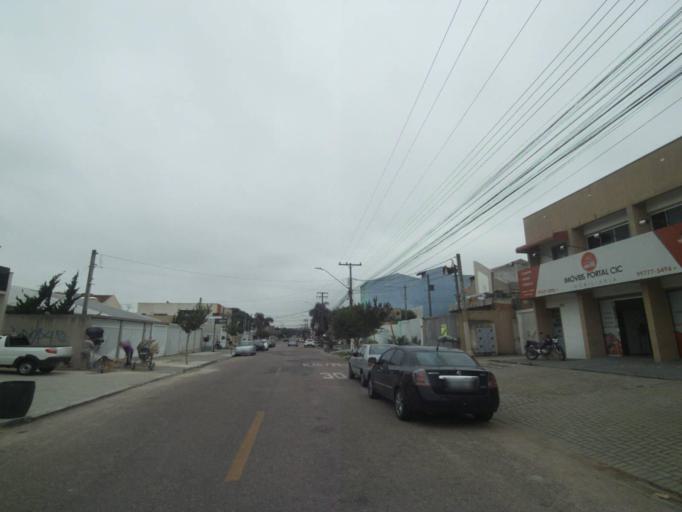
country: BR
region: Parana
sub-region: Araucaria
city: Araucaria
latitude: -25.5497
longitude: -49.3394
